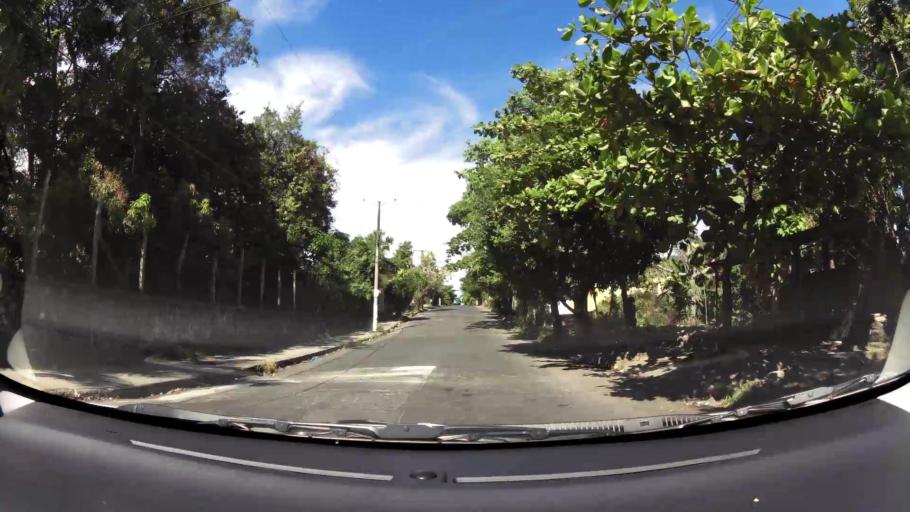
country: SV
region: San Salvador
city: Apopa
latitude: 13.8059
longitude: -89.1766
